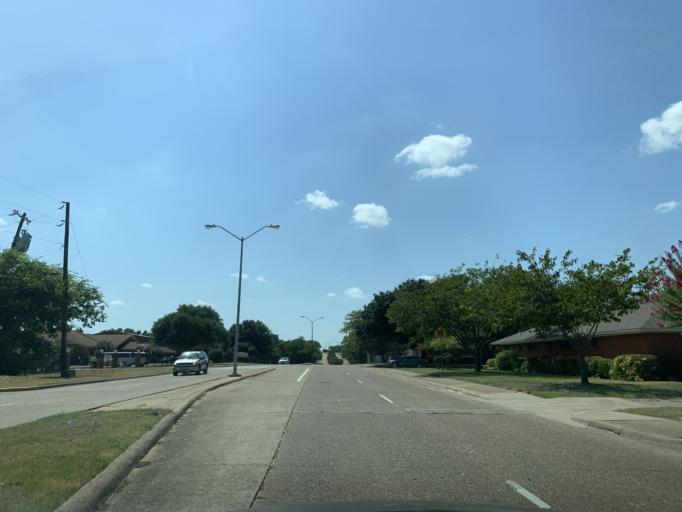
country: US
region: Texas
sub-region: Dallas County
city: Lancaster
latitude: 32.6750
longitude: -96.8074
